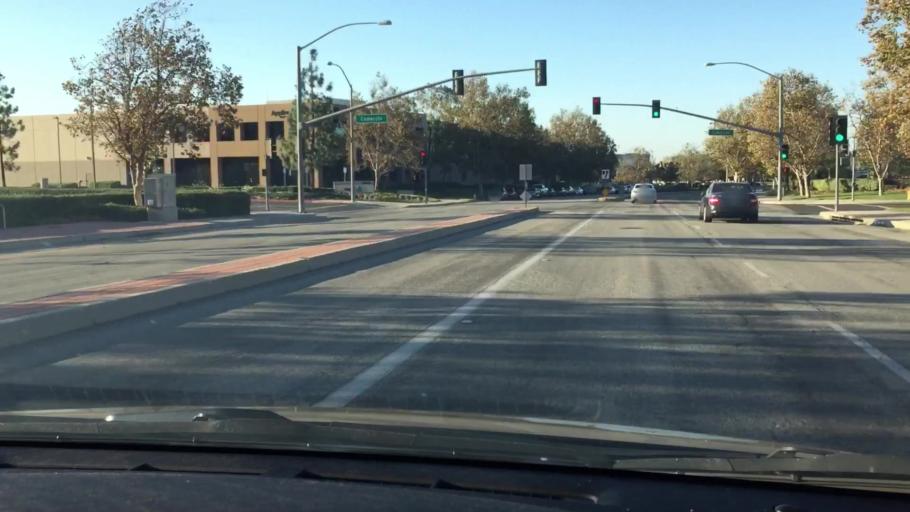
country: US
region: California
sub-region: Orange County
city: Rancho Santa Margarita
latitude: 33.6336
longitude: -117.6039
